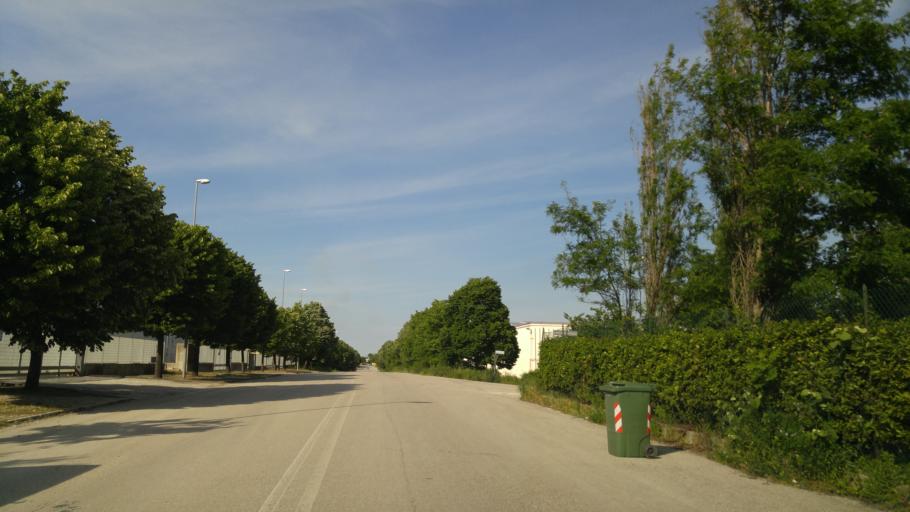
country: IT
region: The Marches
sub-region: Provincia di Pesaro e Urbino
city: Bellocchi
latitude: 43.7955
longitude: 13.0102
